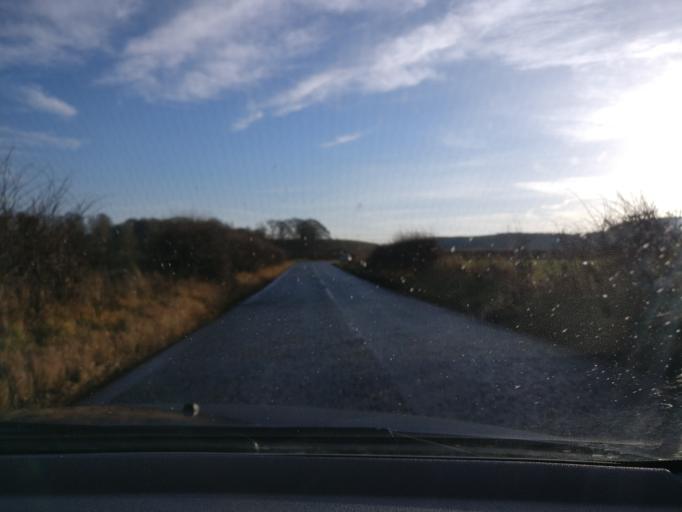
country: GB
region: Scotland
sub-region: The Scottish Borders
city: Kelso
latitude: 55.5359
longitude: -2.4531
